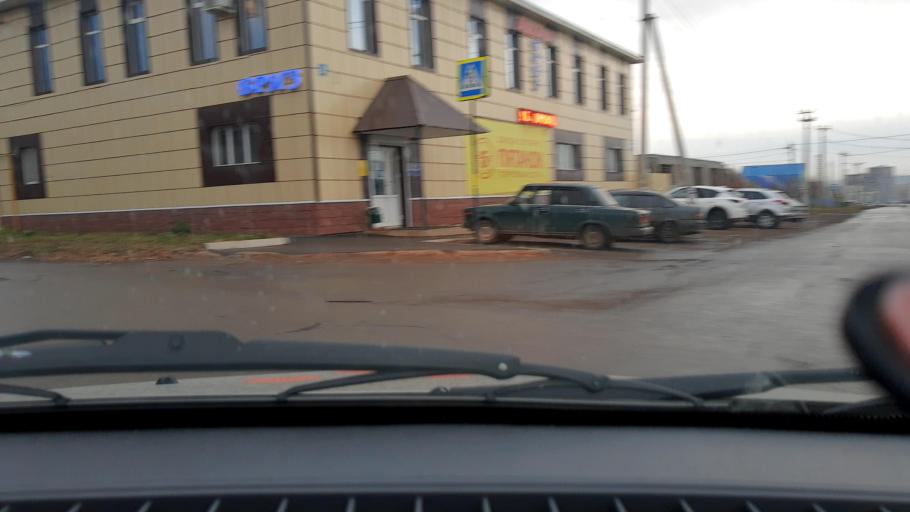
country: RU
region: Bashkortostan
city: Avdon
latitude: 54.6882
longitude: 55.8012
